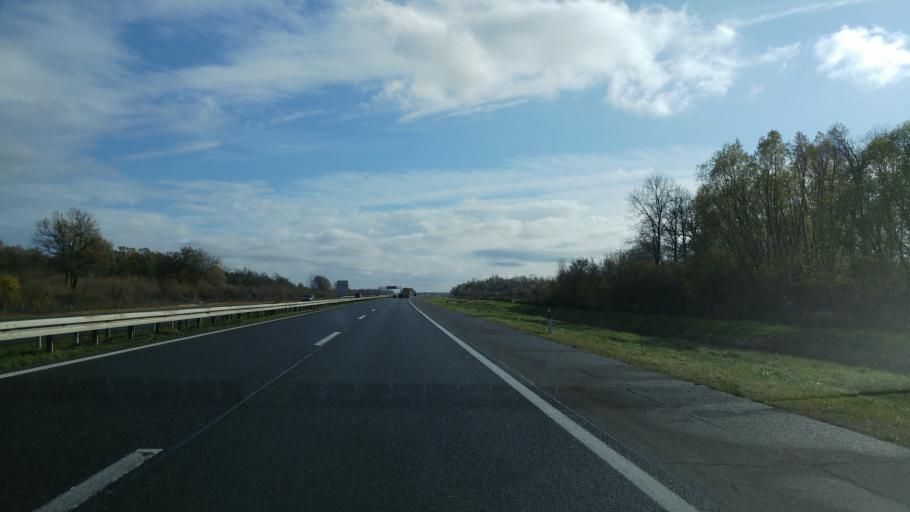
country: HR
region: Grad Zagreb
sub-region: Sesvete
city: Sesvete
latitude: 45.7859
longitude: 16.1809
